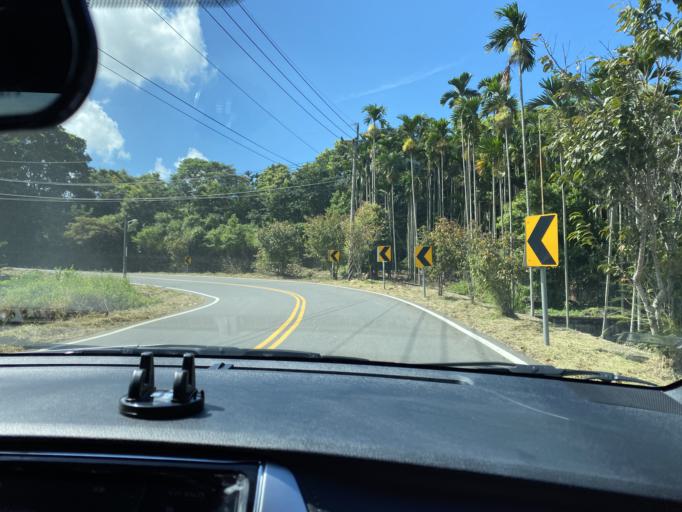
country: TW
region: Taiwan
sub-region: Nantou
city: Nantou
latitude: 23.8659
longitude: 120.6322
